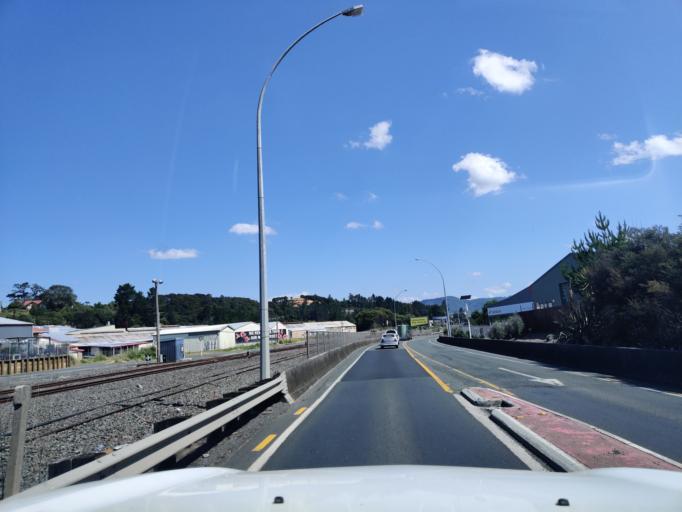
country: NZ
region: Waikato
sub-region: Waikato District
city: Ngaruawahia
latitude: -37.5617
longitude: 175.1596
